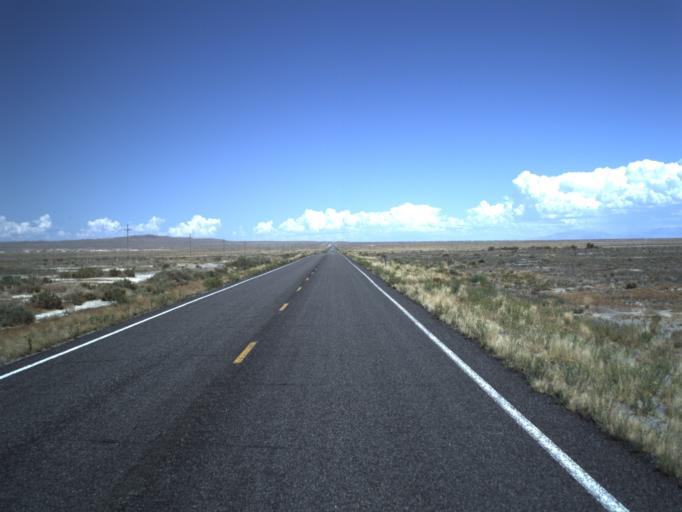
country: US
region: Utah
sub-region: Millard County
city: Delta
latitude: 39.1014
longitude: -113.1527
